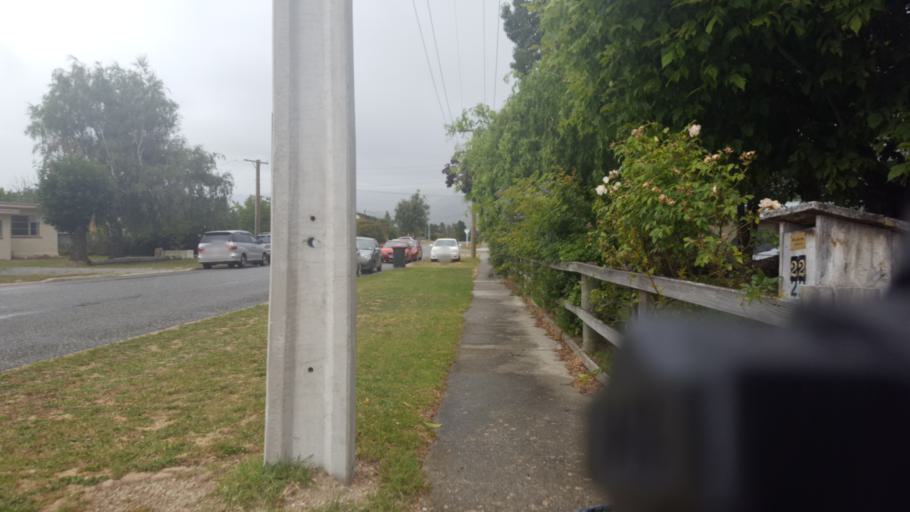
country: NZ
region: Otago
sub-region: Queenstown-Lakes District
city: Wanaka
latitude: -45.1901
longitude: 169.3286
